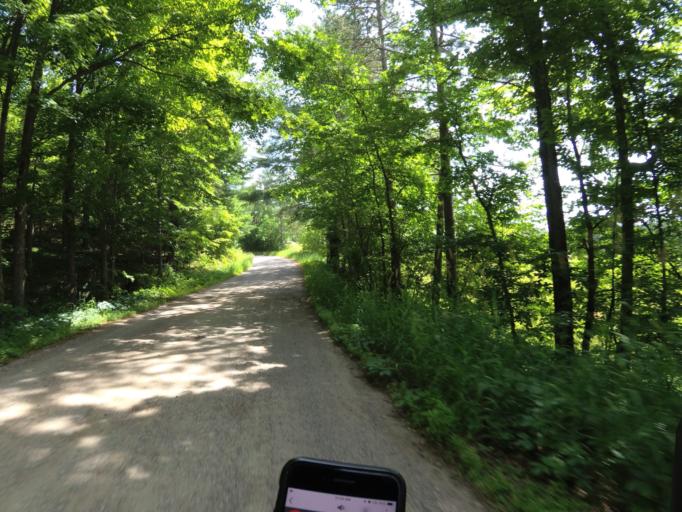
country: CA
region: Ontario
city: Skatepark
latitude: 44.7360
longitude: -76.8413
